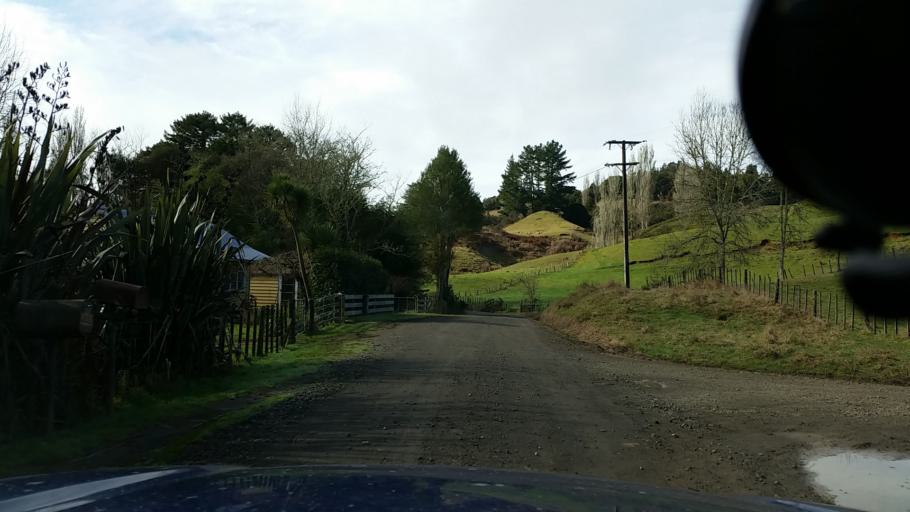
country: NZ
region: Taranaki
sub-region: New Plymouth District
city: Waitara
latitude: -39.0339
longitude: 174.7969
